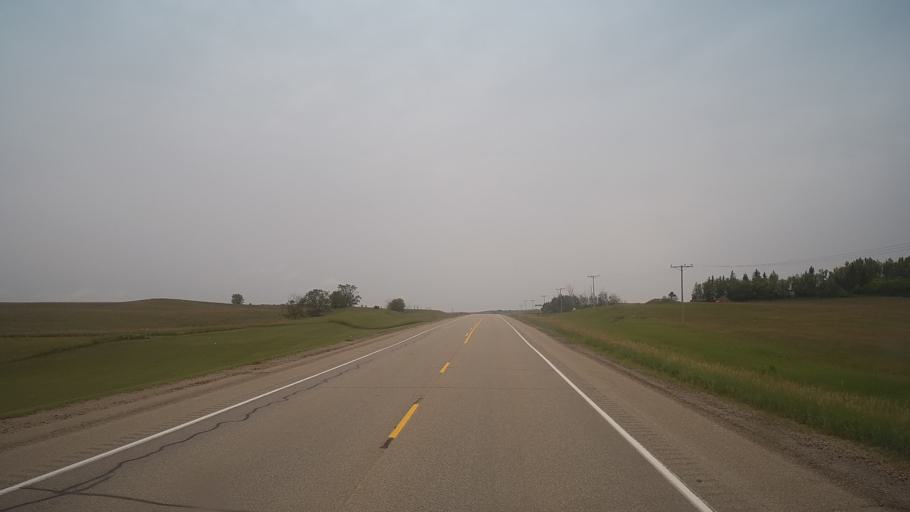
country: CA
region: Saskatchewan
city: Biggar
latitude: 52.0564
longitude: -107.8543
